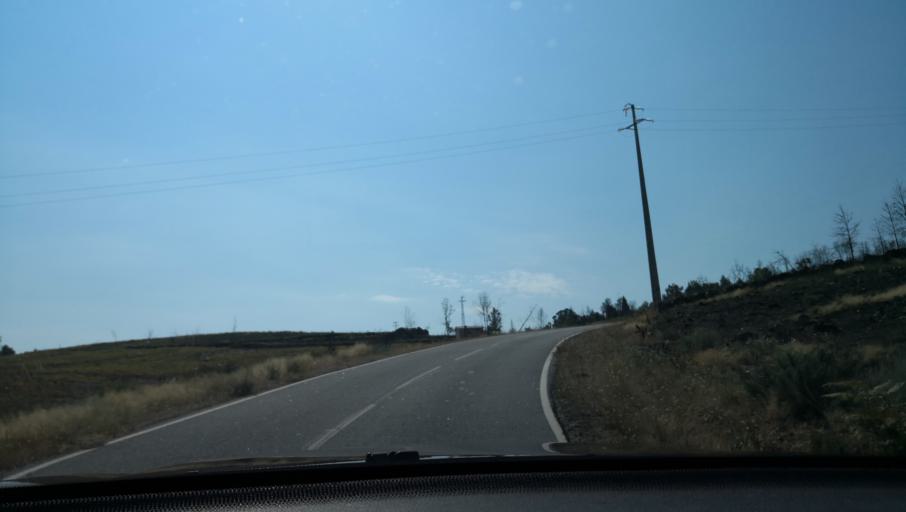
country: PT
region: Vila Real
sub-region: Sabrosa
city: Sabrosa
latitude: 41.3402
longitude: -7.5943
